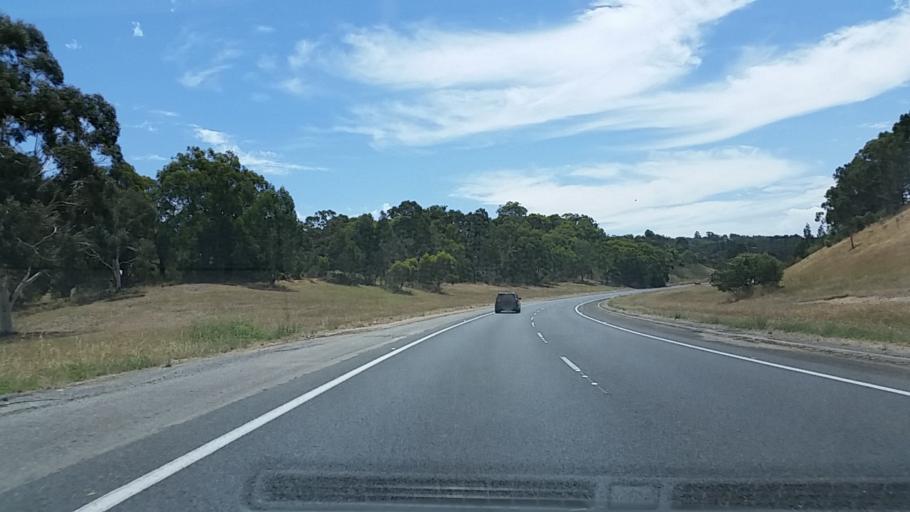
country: AU
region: South Australia
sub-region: Mount Barker
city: Hahndorf
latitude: -35.0235
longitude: 138.7857
